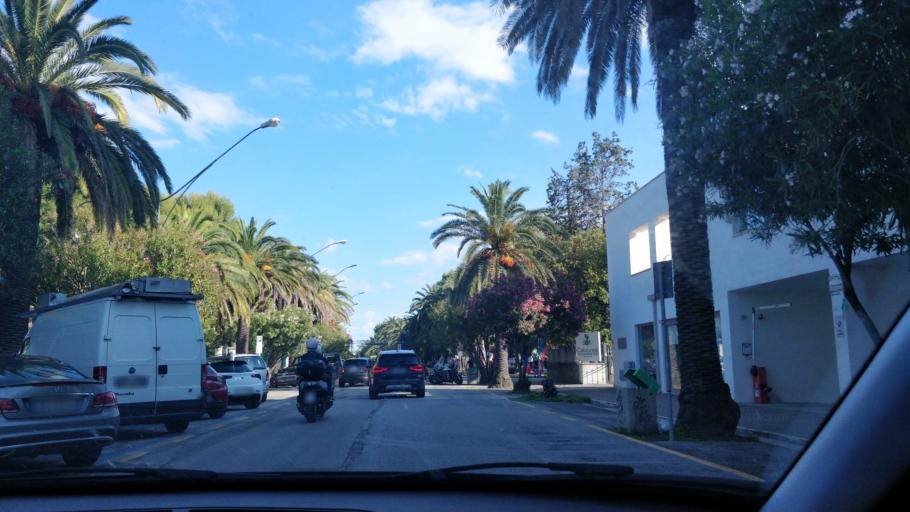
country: IT
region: The Marches
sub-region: Provincia di Ascoli Piceno
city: Grottammare
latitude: 42.9532
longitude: 13.8853
